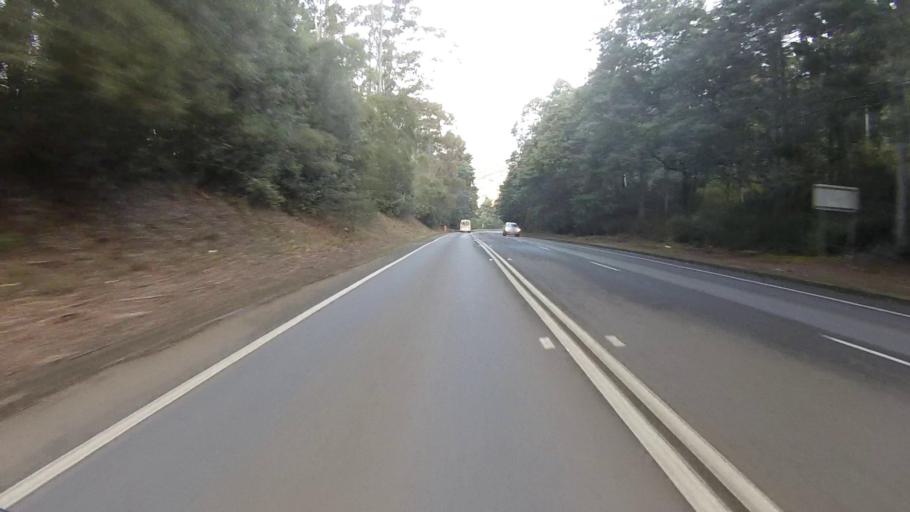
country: AU
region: Tasmania
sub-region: Sorell
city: Sorell
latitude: -43.0077
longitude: 147.9267
